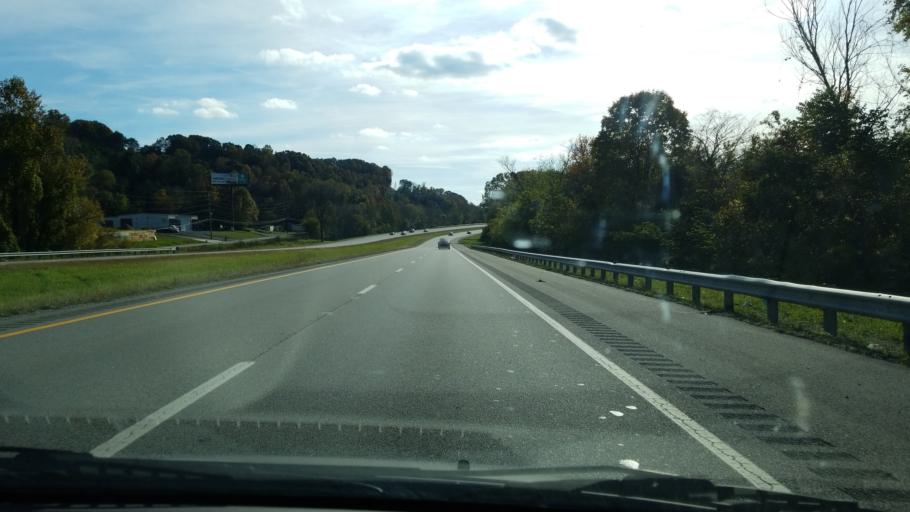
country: US
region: Tennessee
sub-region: Hamilton County
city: Soddy-Daisy
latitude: 35.2439
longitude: -85.1825
